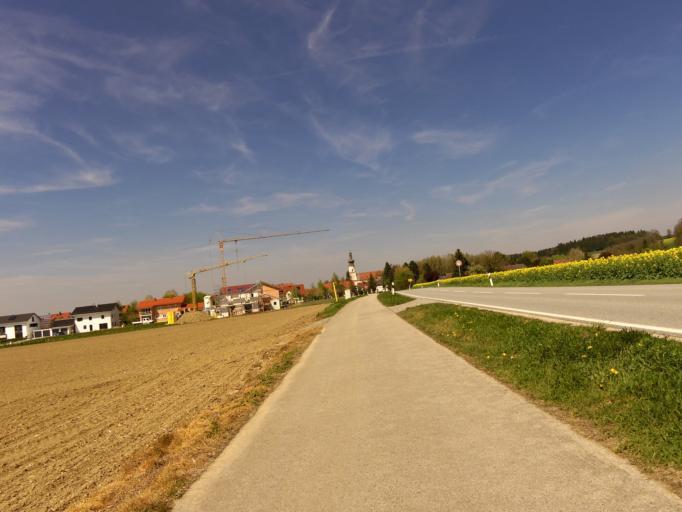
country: DE
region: Bavaria
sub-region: Upper Bavaria
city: Bockhorn
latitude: 48.3103
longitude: 11.9865
